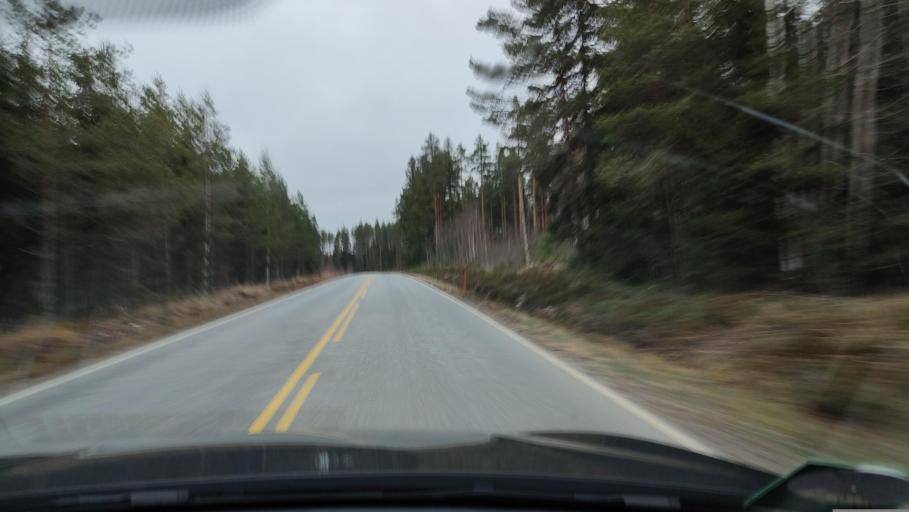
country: FI
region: Southern Ostrobothnia
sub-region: Suupohja
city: Karijoki
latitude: 62.2407
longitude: 21.7585
